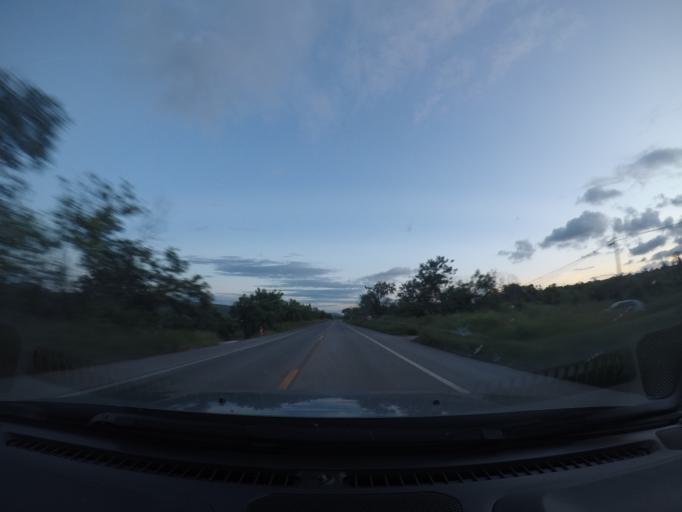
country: BR
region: Bahia
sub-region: Seabra
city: Seabra
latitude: -12.4398
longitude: -41.7541
